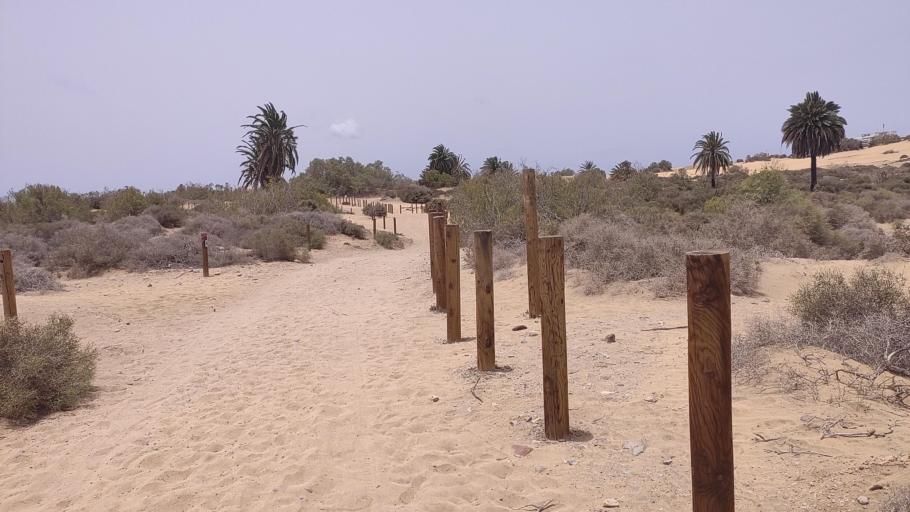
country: ES
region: Canary Islands
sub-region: Provincia de Las Palmas
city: Playa del Ingles
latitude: 27.7421
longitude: -15.5897
